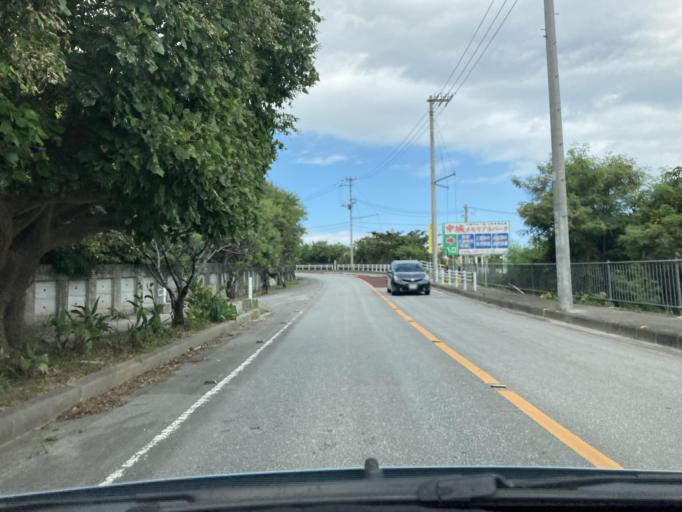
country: JP
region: Okinawa
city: Ginowan
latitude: 26.2651
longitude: 127.7856
